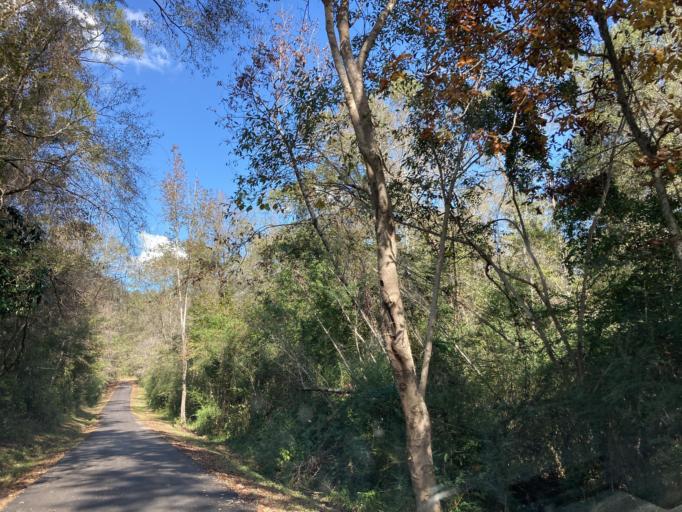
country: US
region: Mississippi
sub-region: Lamar County
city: Purvis
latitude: 31.2352
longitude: -89.4295
